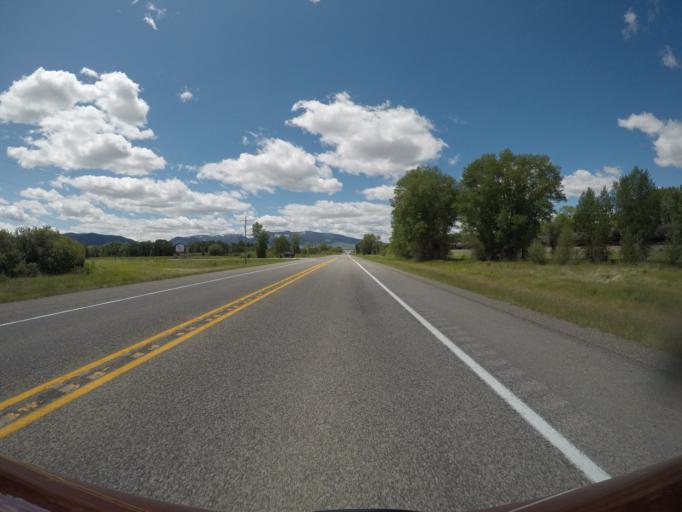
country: US
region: Montana
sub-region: Park County
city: Livingston
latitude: 45.6790
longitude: -110.5265
